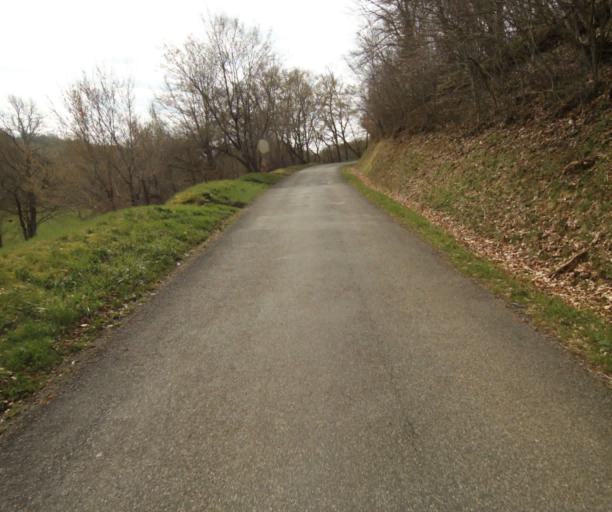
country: FR
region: Limousin
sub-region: Departement de la Correze
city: Laguenne
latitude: 45.2431
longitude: 1.8435
